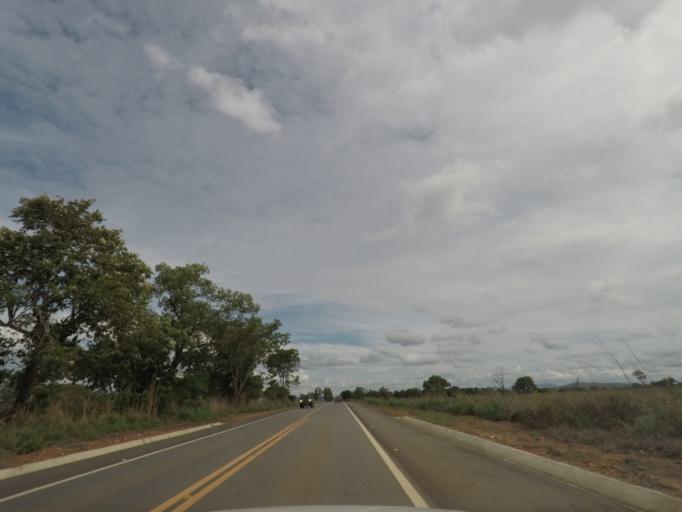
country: BR
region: Goias
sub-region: Uruacu
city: Uruacu
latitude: -14.7196
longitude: -49.0825
